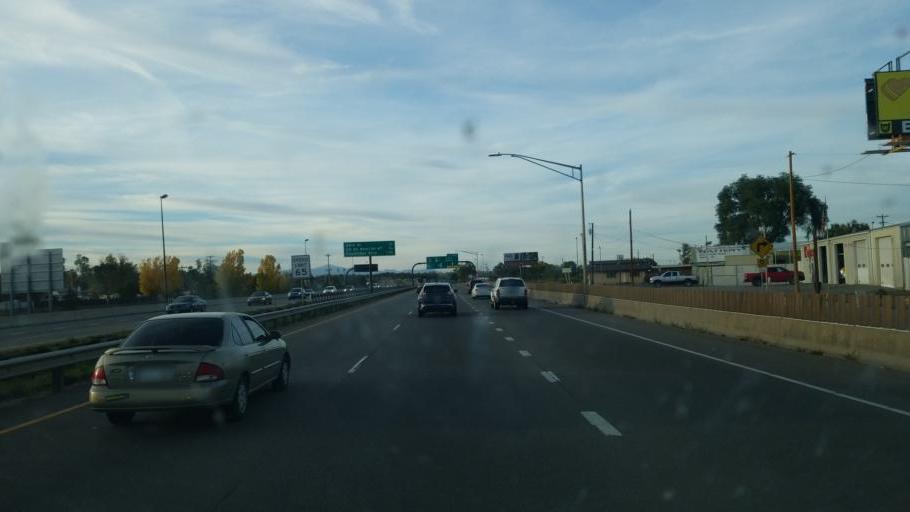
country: US
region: Colorado
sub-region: Pueblo County
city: Pueblo
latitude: 38.2921
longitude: -104.6082
